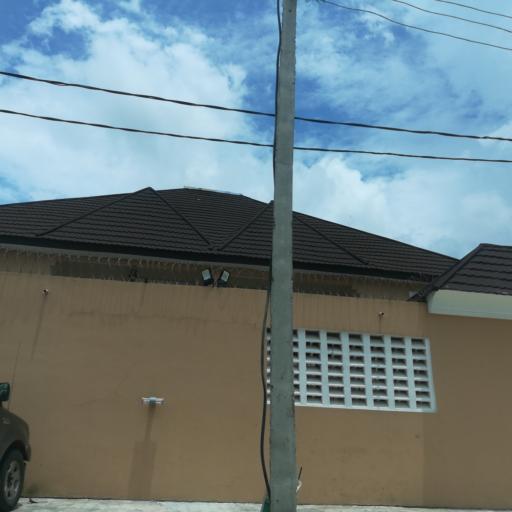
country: NG
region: Lagos
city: Ikoyi
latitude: 6.4410
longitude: 3.4658
